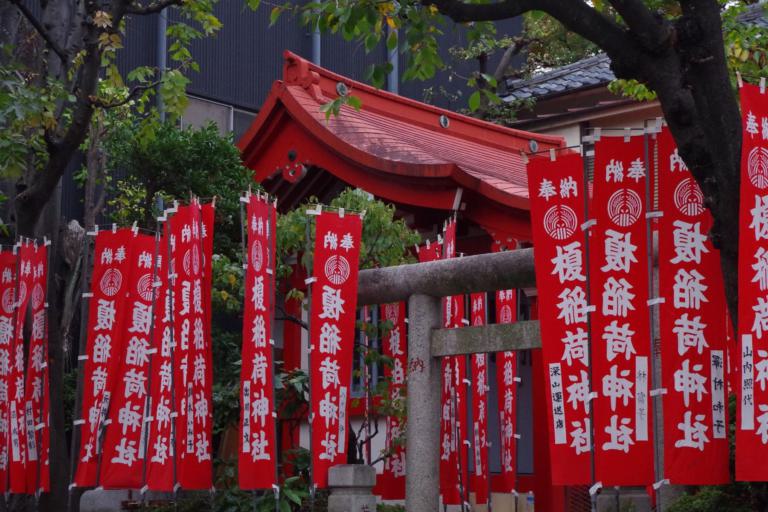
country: JP
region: Tokyo
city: Urayasu
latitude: 35.6910
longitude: 139.8070
